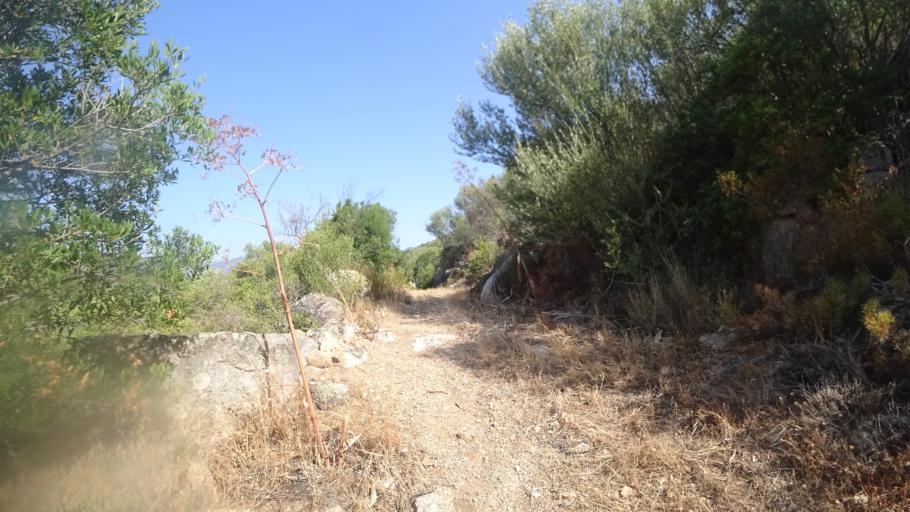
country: FR
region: Corsica
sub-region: Departement de la Corse-du-Sud
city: Porto-Vecchio
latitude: 41.6647
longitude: 9.3264
